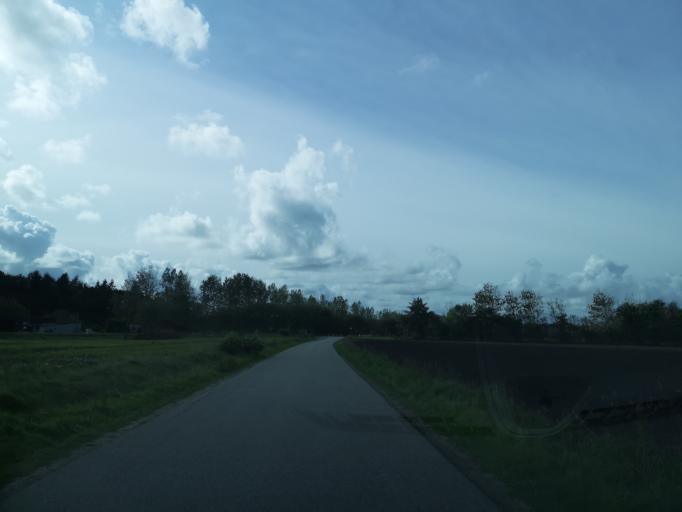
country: DK
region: Central Jutland
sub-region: Ringkobing-Skjern Kommune
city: Skjern
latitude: 55.9437
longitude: 8.5296
